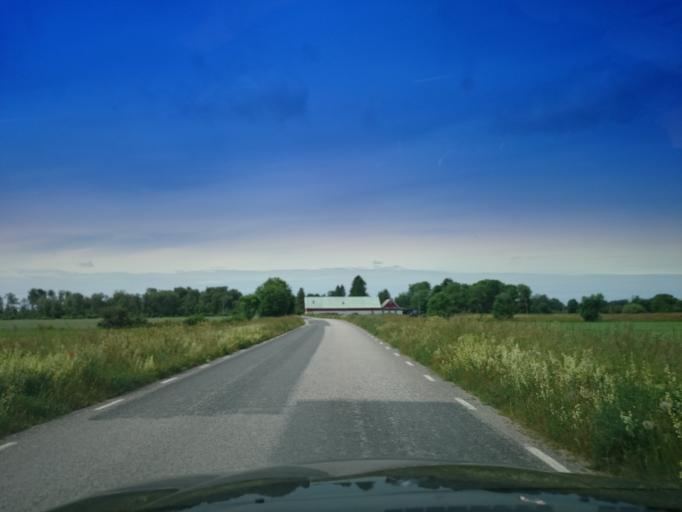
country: SE
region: Gotland
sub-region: Gotland
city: Hemse
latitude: 57.2457
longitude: 18.5245
